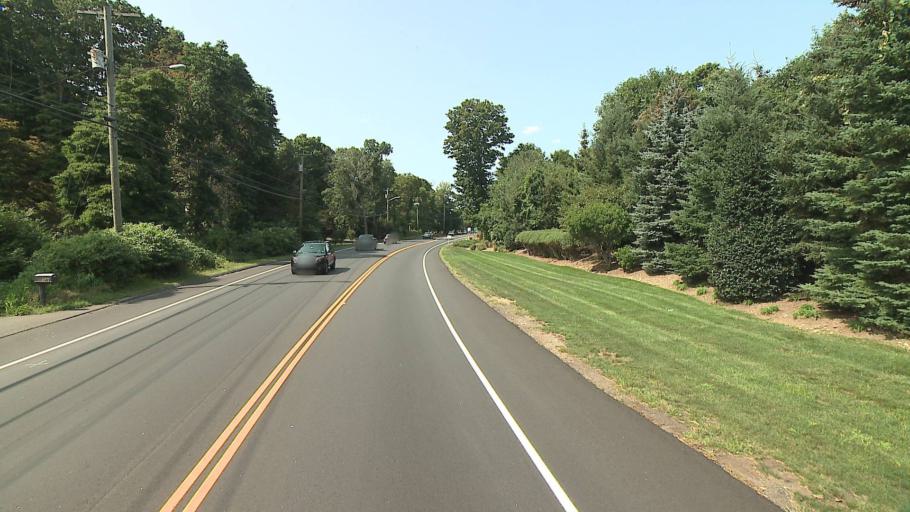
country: US
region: Connecticut
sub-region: Fairfield County
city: Trumbull
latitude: 41.2901
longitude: -73.2417
